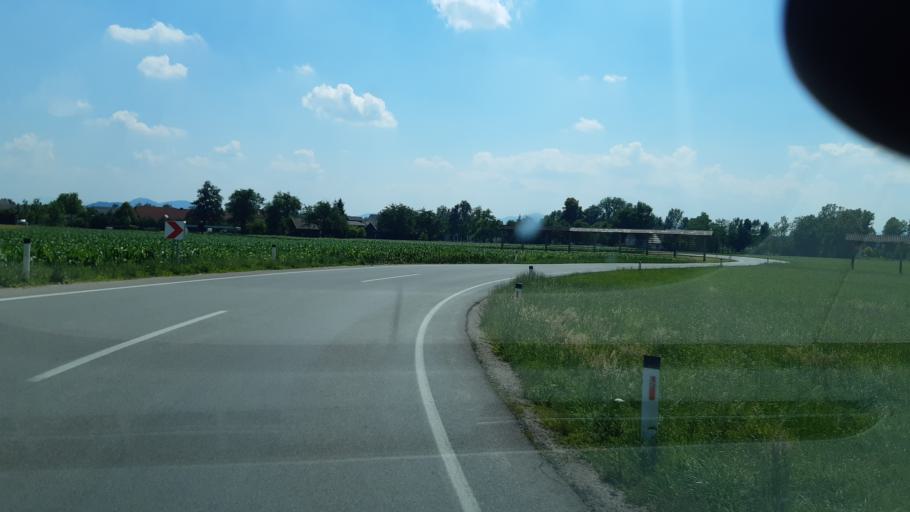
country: SI
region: Cerklje na Gorenjskem
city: Cerklje na Gorenjskem
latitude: 46.2434
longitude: 14.4870
